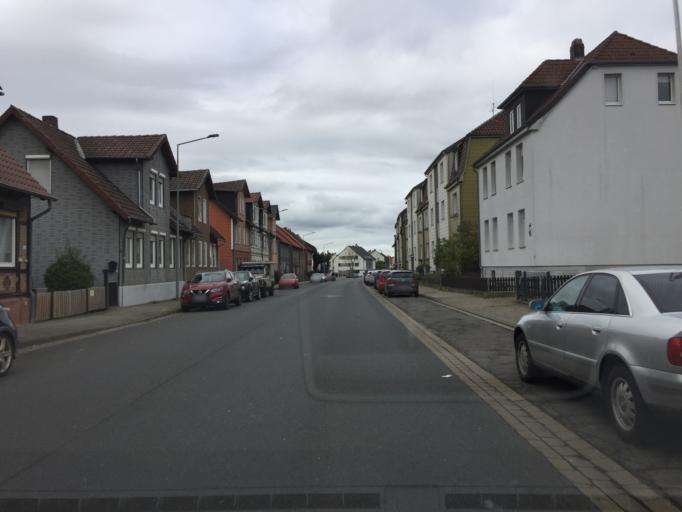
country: DE
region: Lower Saxony
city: Wolfenbuettel
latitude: 52.1673
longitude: 10.5190
